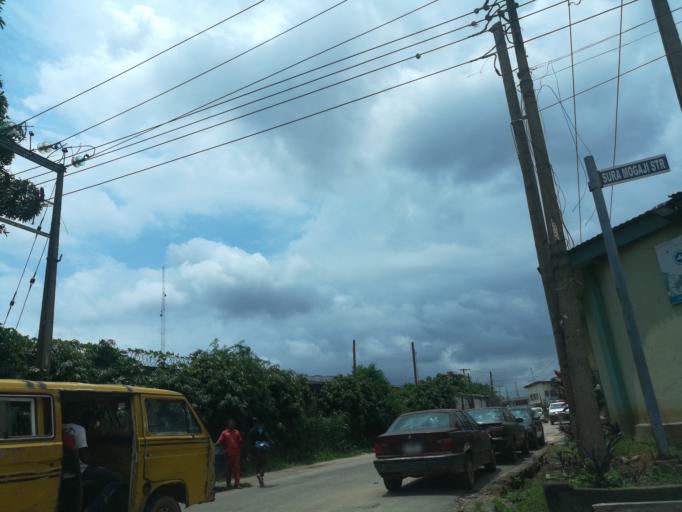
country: NG
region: Lagos
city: Somolu
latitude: 6.5478
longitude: 3.3578
